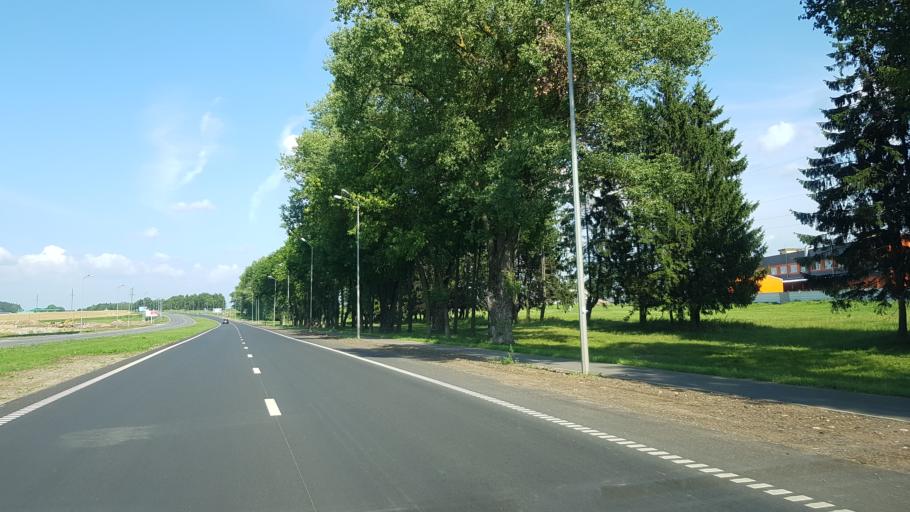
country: BY
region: Minsk
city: Dzyarzhynsk
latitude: 53.6888
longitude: 27.1598
